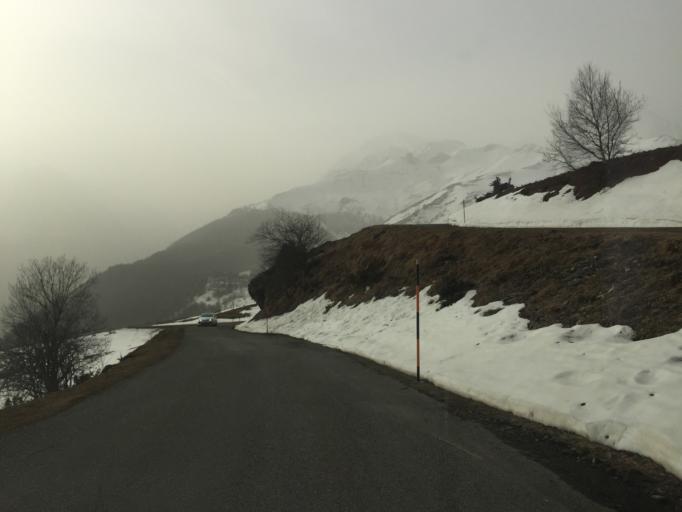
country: FR
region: Midi-Pyrenees
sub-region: Departement des Hautes-Pyrenees
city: Saint-Lary-Soulan
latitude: 42.8010
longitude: 0.3880
